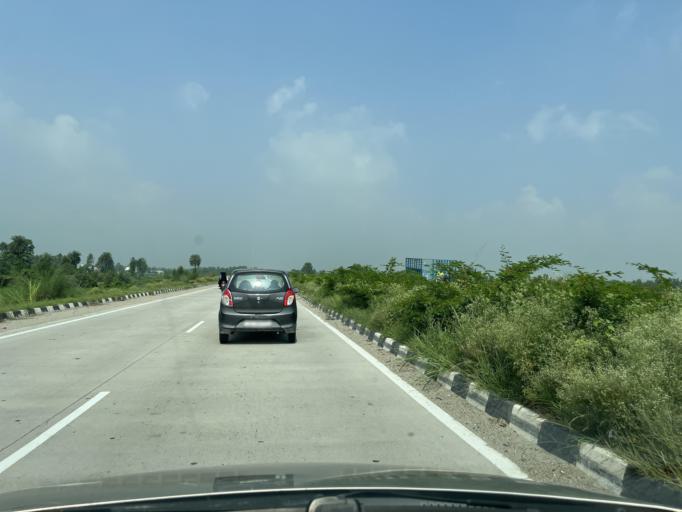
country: IN
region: Uttarakhand
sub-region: Udham Singh Nagar
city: Kashipur
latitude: 29.1635
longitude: 78.9945
